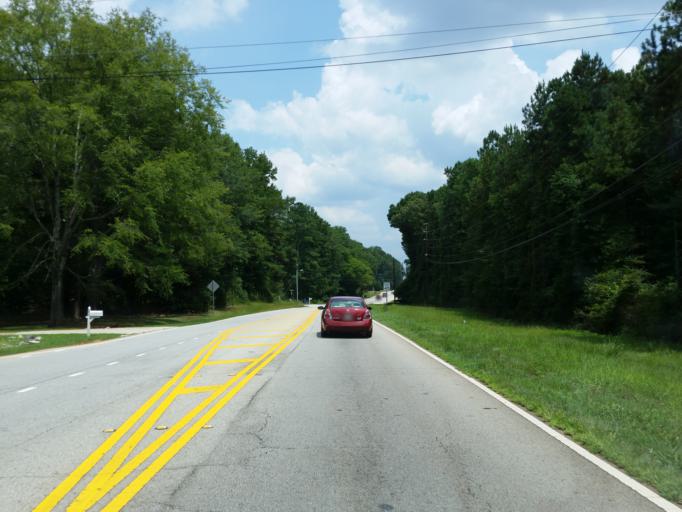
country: US
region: Georgia
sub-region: Henry County
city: Stockbridge
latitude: 33.5000
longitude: -84.2567
